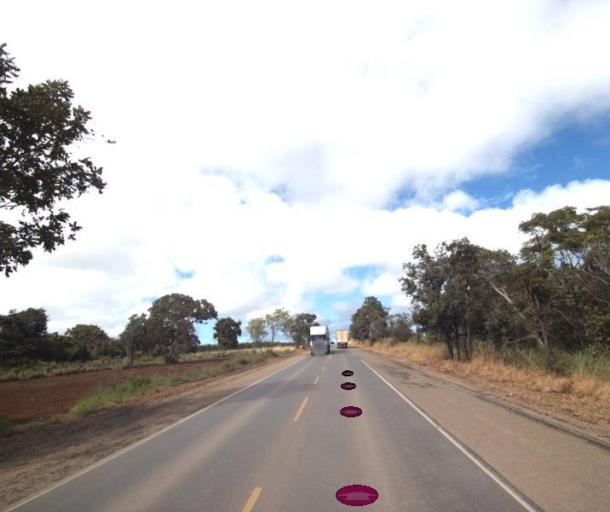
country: BR
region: Goias
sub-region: Uruacu
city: Uruacu
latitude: -14.7585
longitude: -49.2583
